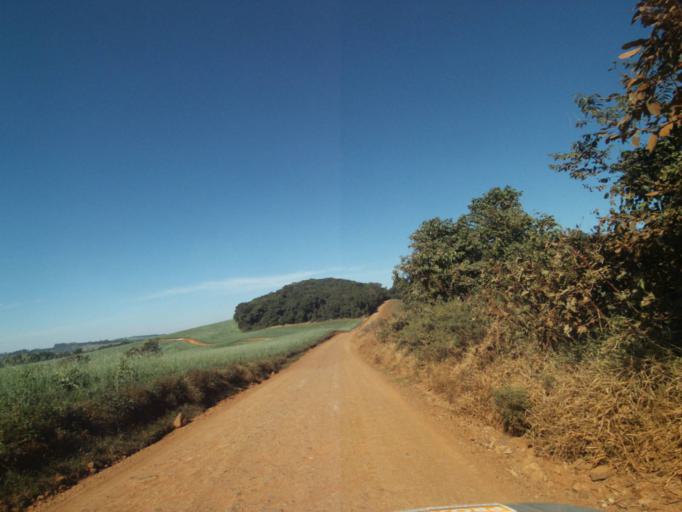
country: BR
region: Parana
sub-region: Tibagi
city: Tibagi
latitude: -24.5874
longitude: -50.6079
